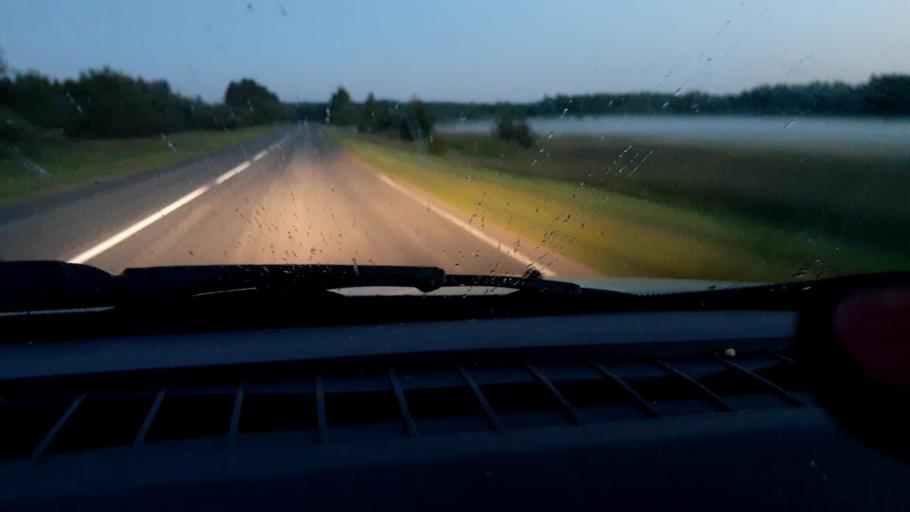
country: RU
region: Nizjnij Novgorod
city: Tonkino
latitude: 57.3143
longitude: 46.4691
